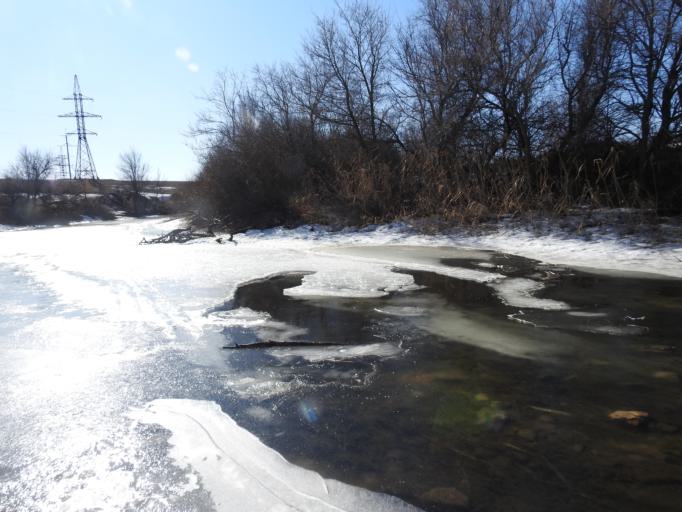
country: RU
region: Saratov
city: Yershov
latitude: 51.3544
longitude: 48.2353
